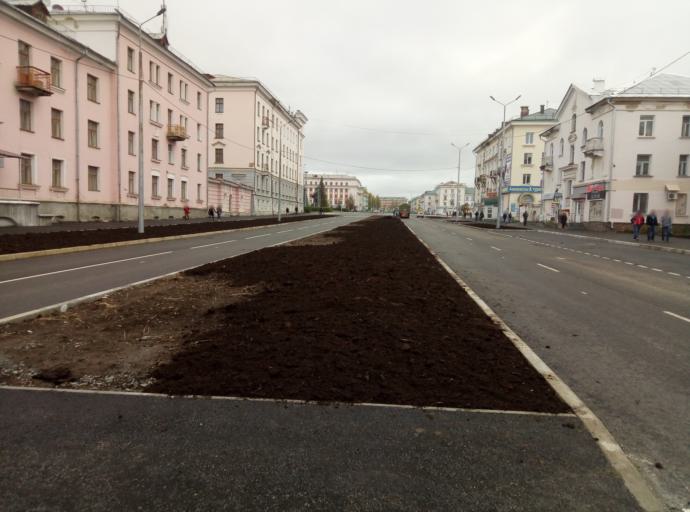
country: RU
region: Sverdlovsk
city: Krasnotur'insk
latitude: 59.7638
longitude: 60.1899
